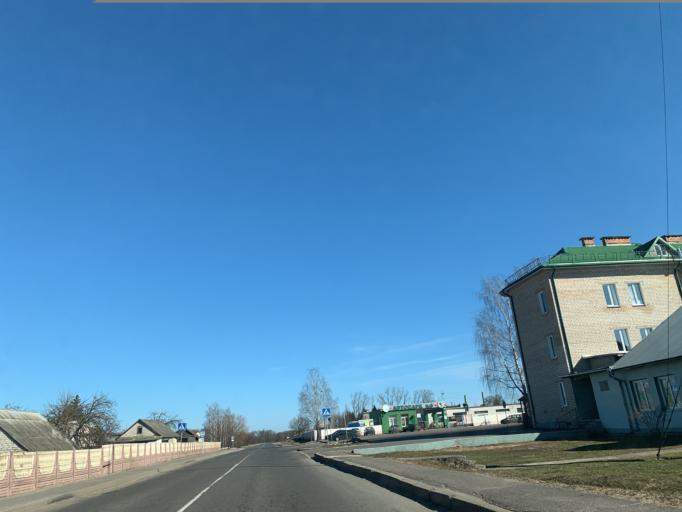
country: BY
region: Minsk
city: Nyasvizh
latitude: 53.2148
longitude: 26.6993
